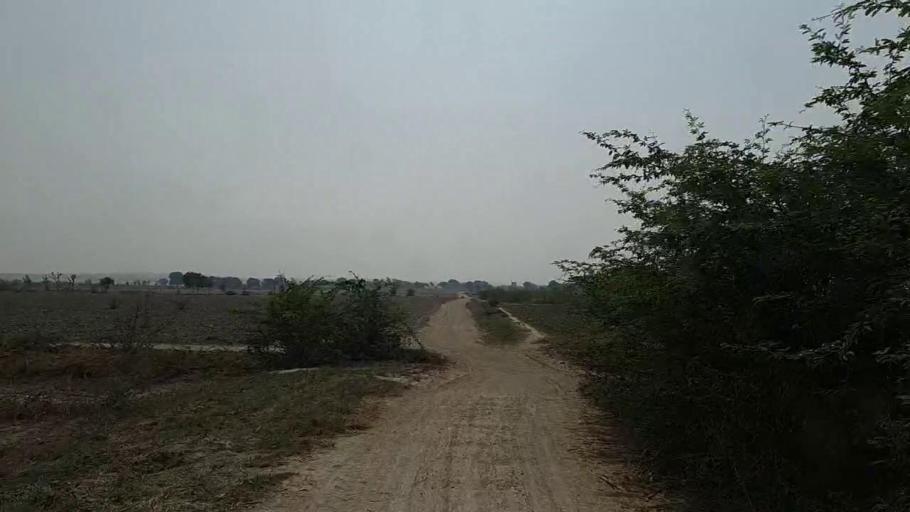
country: PK
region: Sindh
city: Naukot
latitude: 24.8112
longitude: 69.3993
